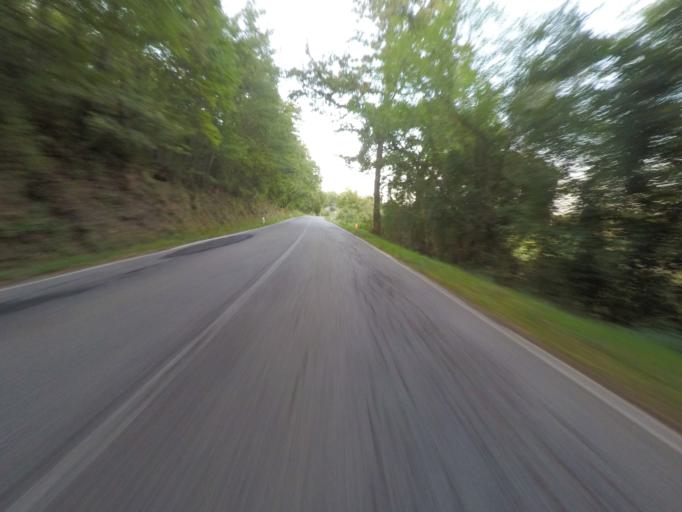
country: IT
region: Tuscany
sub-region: Provincia di Siena
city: Torrita di Siena
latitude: 43.1380
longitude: 11.7326
